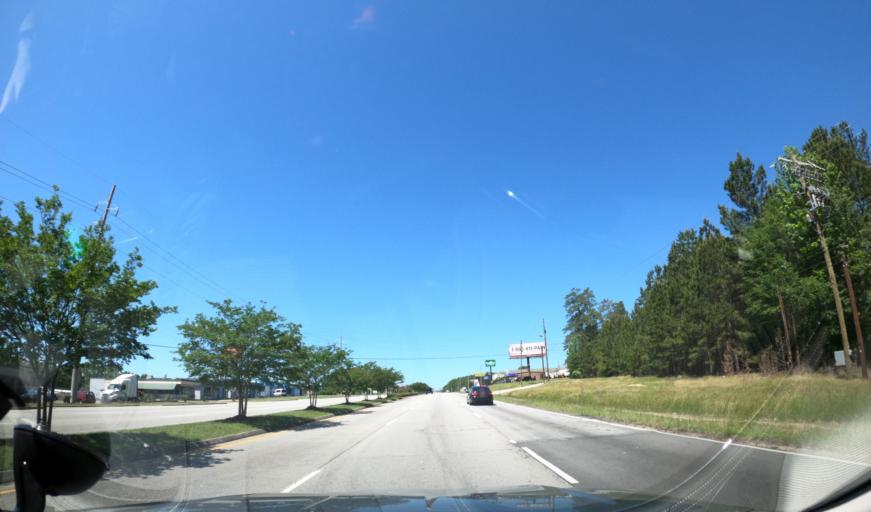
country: US
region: Georgia
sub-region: Columbia County
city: Martinez
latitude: 33.4518
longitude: -82.0603
